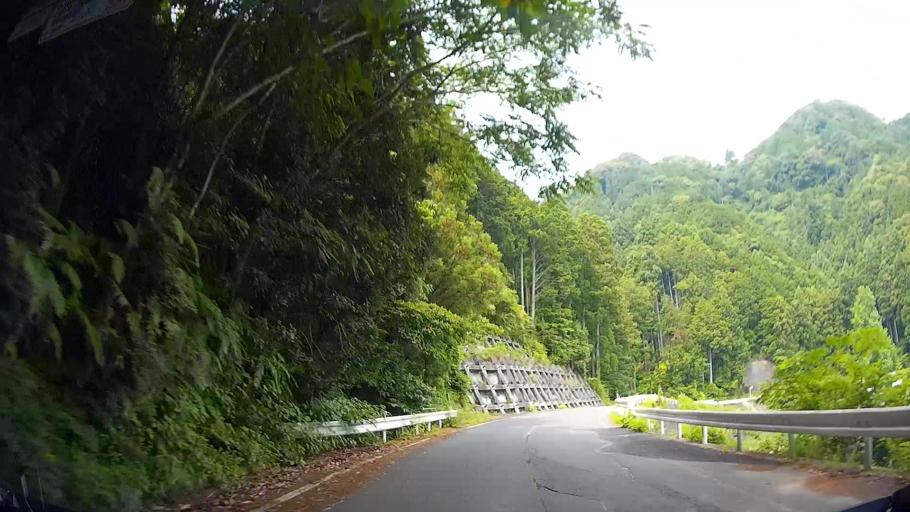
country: JP
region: Shizuoka
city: Hamakita
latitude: 34.9094
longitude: 137.8082
